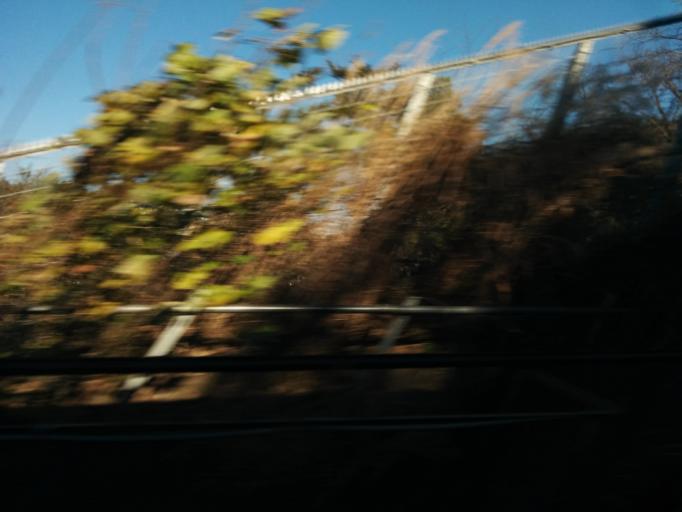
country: JP
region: Kanagawa
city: Atsugi
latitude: 35.4116
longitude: 139.4195
